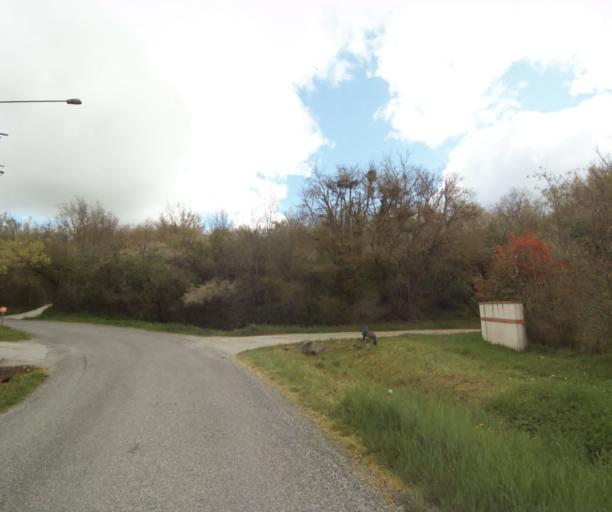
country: FR
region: Midi-Pyrenees
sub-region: Departement de l'Ariege
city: Saverdun
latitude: 43.2243
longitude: 1.5748
